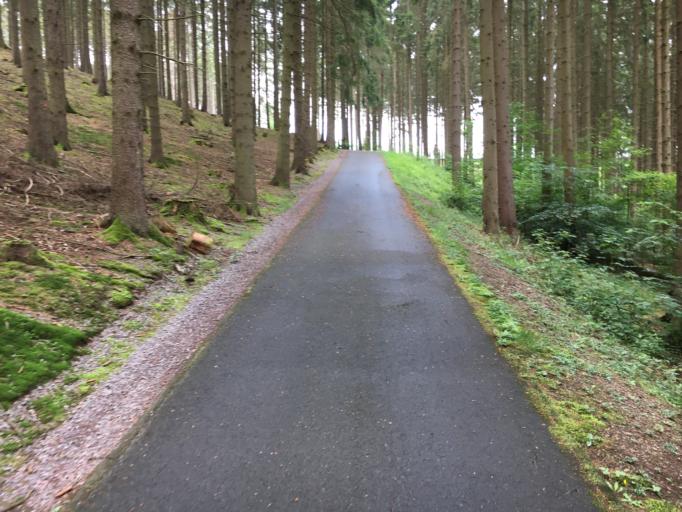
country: DE
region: North Rhine-Westphalia
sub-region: Regierungsbezirk Arnsberg
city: Attendorn
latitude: 51.1147
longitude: 7.8865
